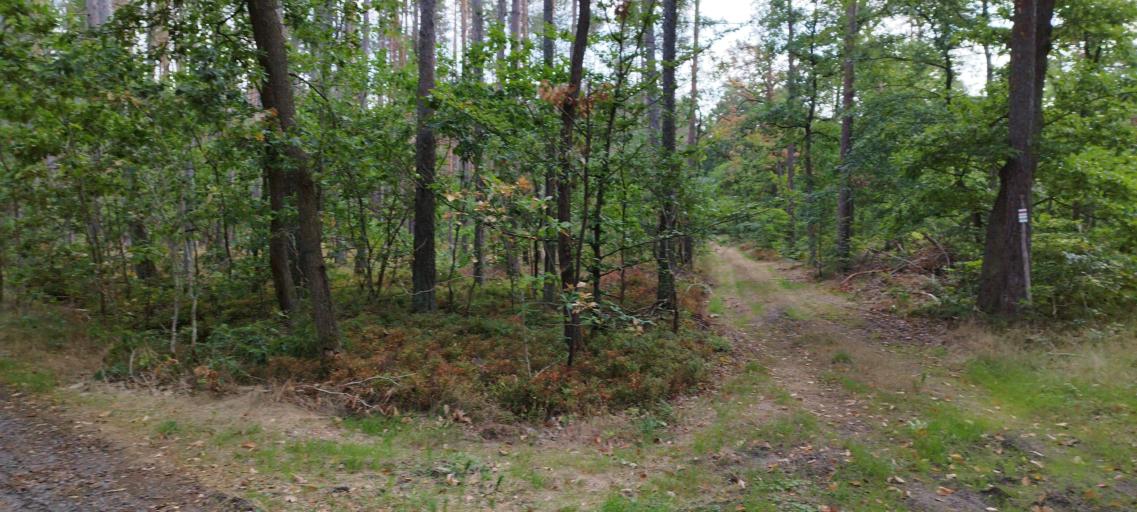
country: DE
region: Brandenburg
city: Premnitz
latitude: 52.5622
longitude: 12.4099
